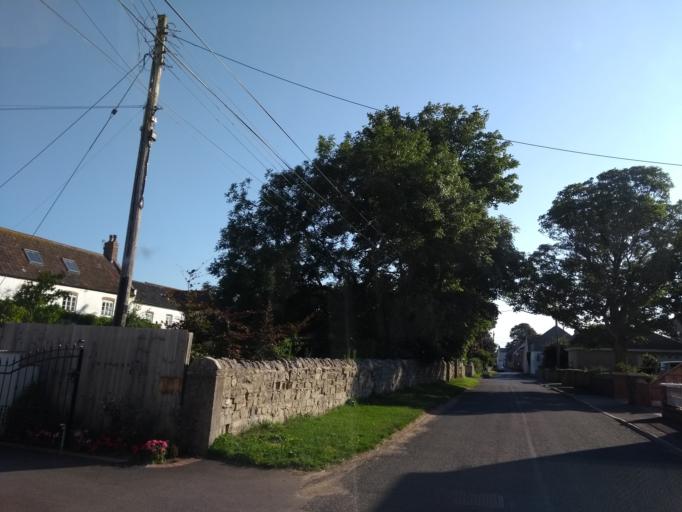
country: GB
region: England
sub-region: Somerset
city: Westonzoyland
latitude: 51.1315
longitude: -2.9477
